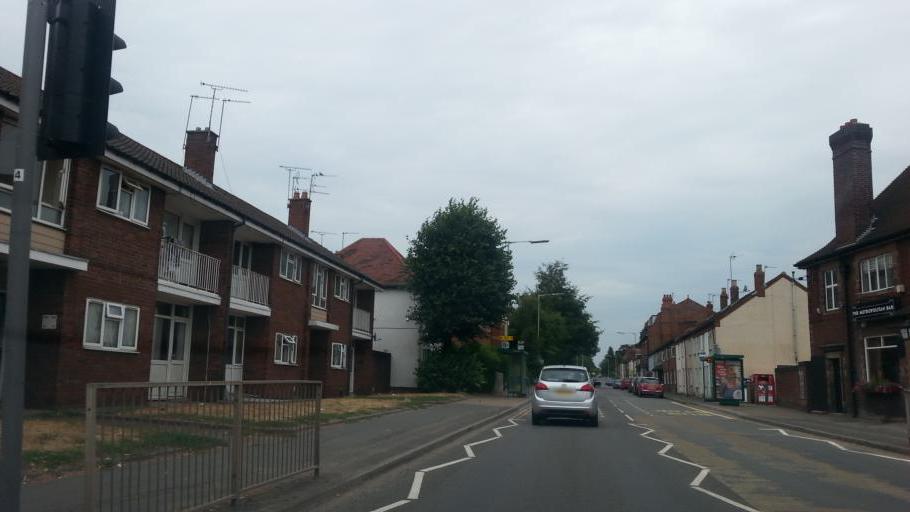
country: GB
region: England
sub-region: Staffordshire
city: Stafford
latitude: 52.8074
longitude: -2.1027
